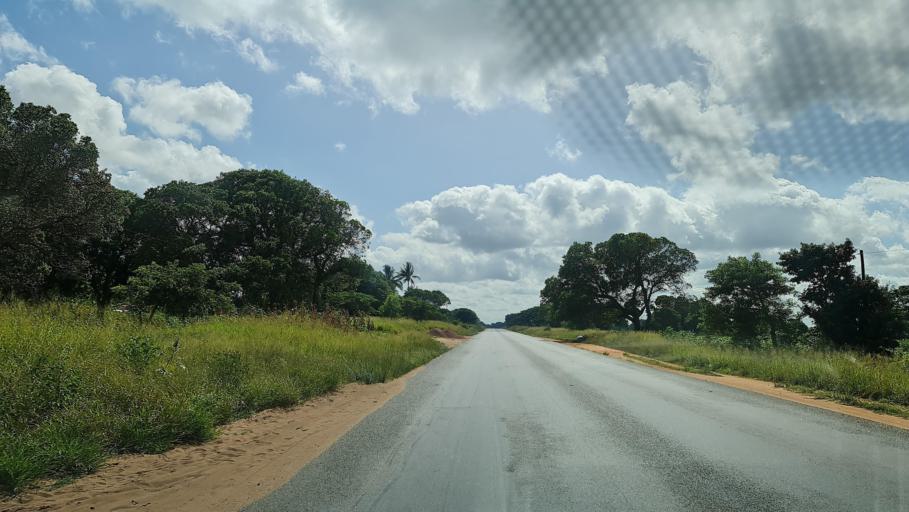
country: MZ
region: Gaza
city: Macia
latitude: -25.0587
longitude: 33.0442
